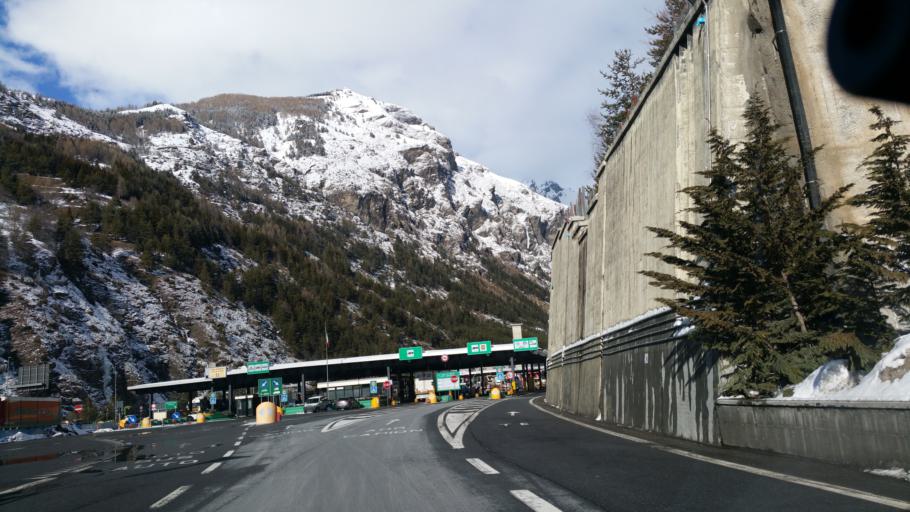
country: IT
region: Piedmont
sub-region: Provincia di Torino
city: Bardonecchia
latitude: 45.0826
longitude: 6.7116
